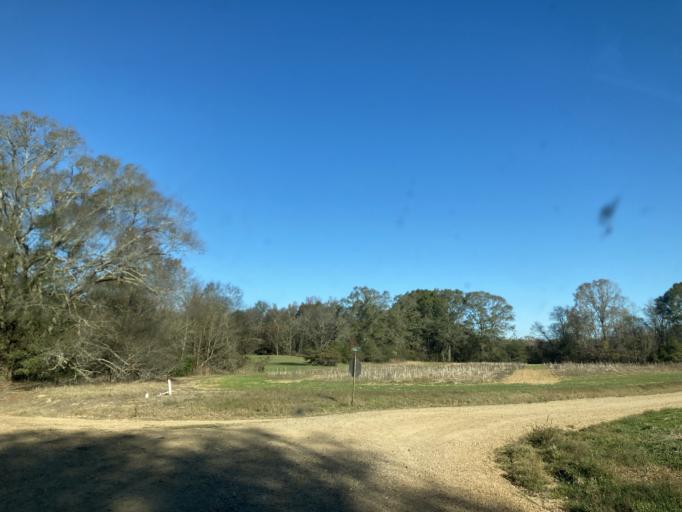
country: US
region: Mississippi
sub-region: Madison County
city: Kearney Park
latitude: 32.7256
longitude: -90.3080
